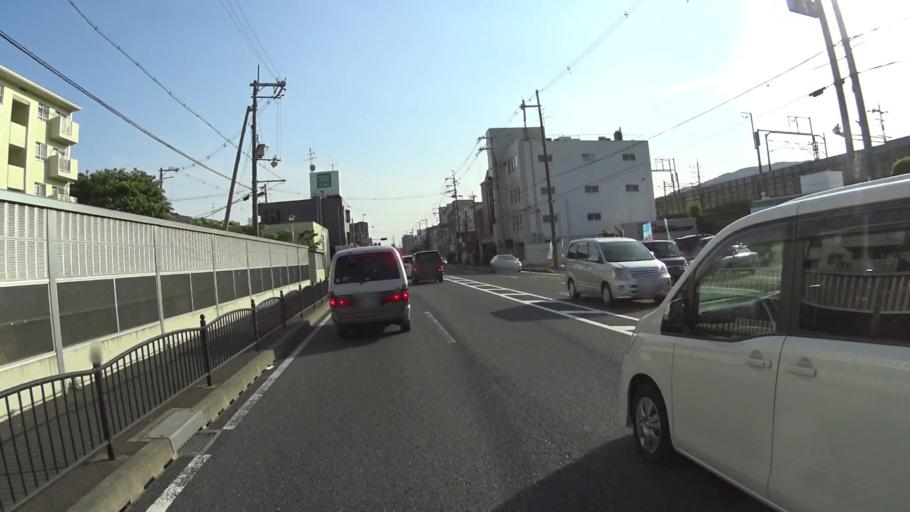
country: JP
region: Kyoto
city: Yawata
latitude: 34.8833
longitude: 135.6742
